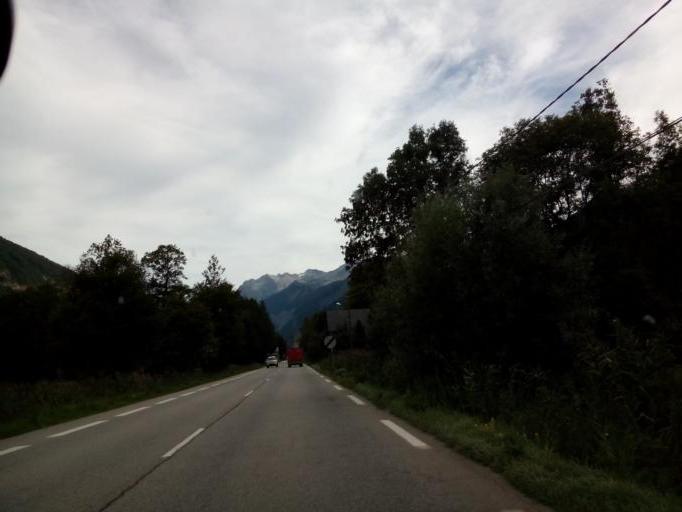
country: FR
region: Rhone-Alpes
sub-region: Departement de l'Isere
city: Huez
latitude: 45.1106
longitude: 6.0067
